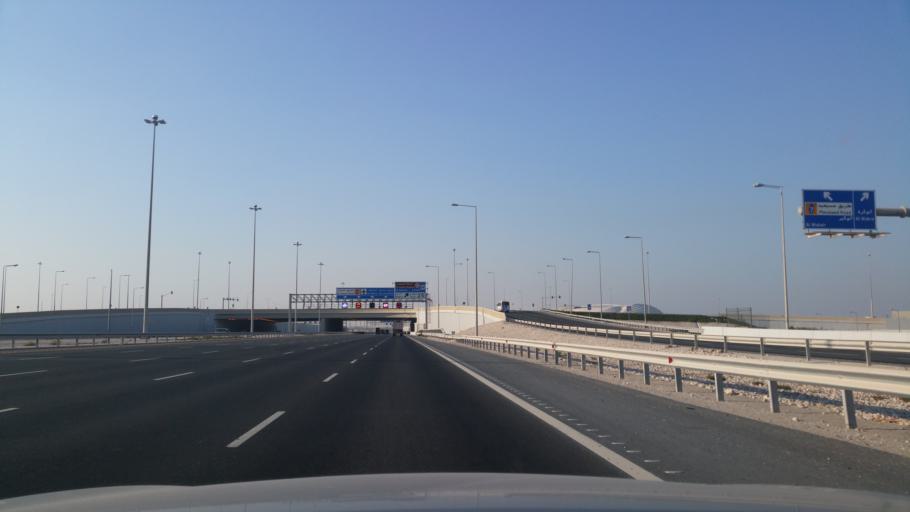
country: QA
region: Al Wakrah
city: Al Wakrah
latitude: 25.1475
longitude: 51.5775
